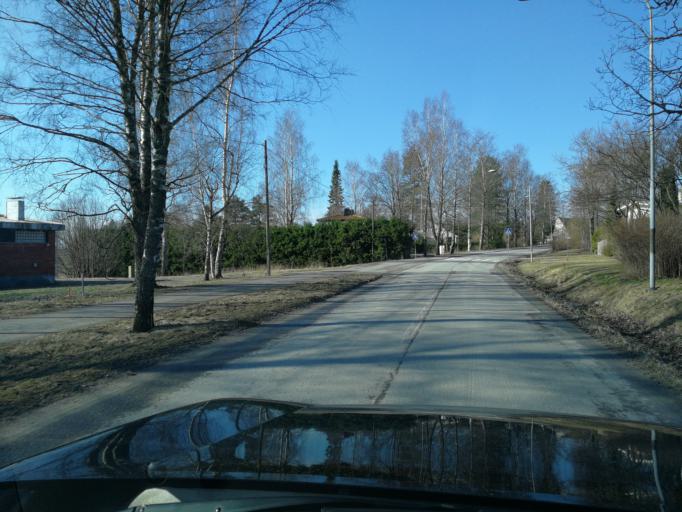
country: FI
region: Uusimaa
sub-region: Raaseporin
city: Inga
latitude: 60.0470
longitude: 24.0094
